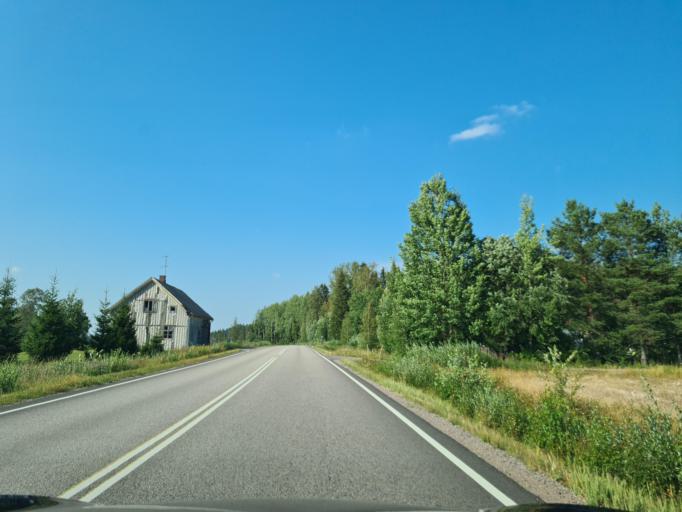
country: FI
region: Satakunta
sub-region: Pohjois-Satakunta
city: Karvia
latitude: 62.2102
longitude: 22.6061
